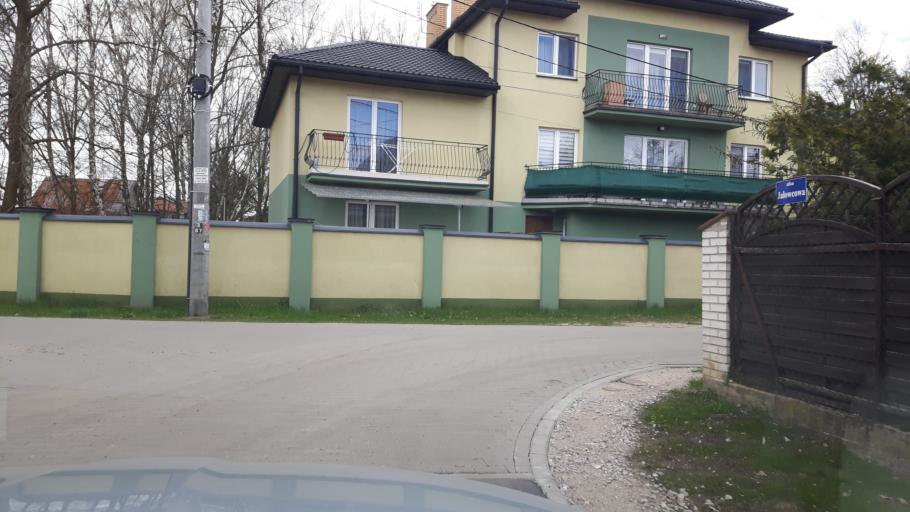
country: PL
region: Masovian Voivodeship
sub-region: Powiat wolominski
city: Kobylka
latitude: 52.3510
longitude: 21.2126
